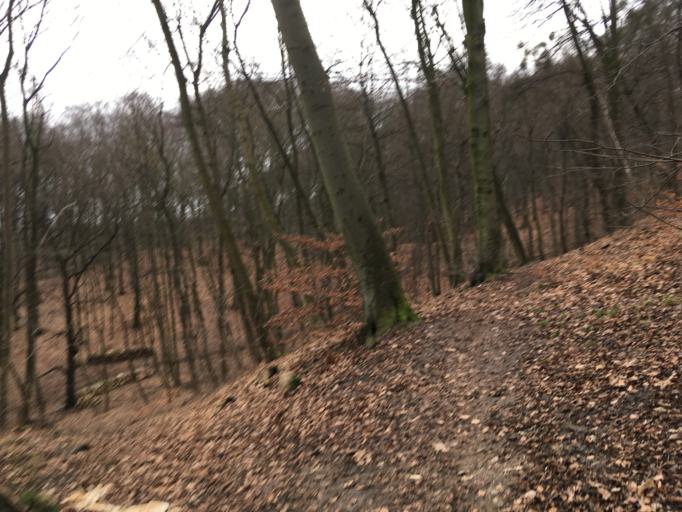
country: PL
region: Pomeranian Voivodeship
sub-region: Gdansk
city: Gdansk
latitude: 54.3729
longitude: 18.6077
